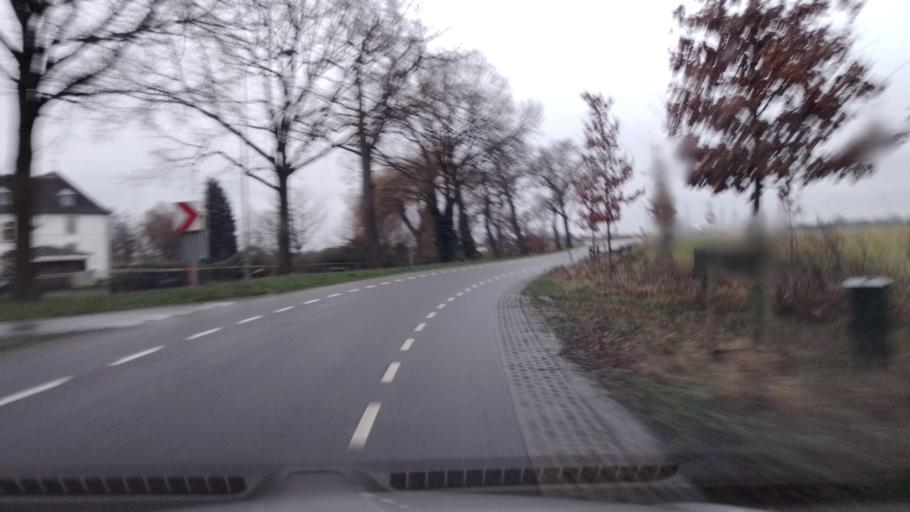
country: NL
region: Limburg
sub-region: Gemeente Bergen
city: Wellerlooi
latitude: 51.5065
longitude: 6.1547
